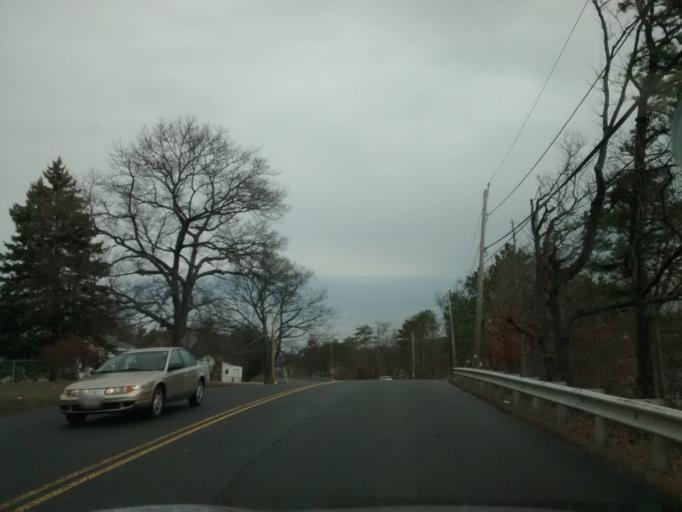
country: US
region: Massachusetts
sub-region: Worcester County
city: Hamilton
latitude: 42.2821
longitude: -71.7577
